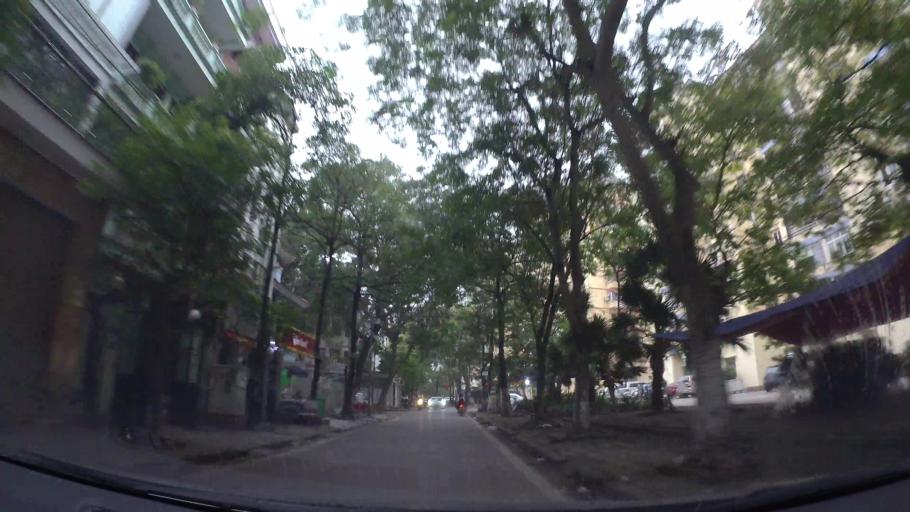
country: VN
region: Ha Noi
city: Thanh Xuan
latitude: 20.9858
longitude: 105.8290
